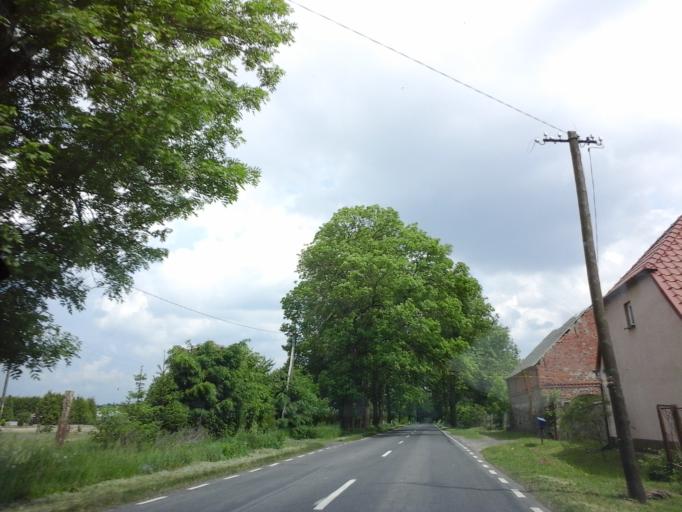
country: PL
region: West Pomeranian Voivodeship
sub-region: Powiat choszczenski
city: Drawno
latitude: 53.2238
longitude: 15.7855
